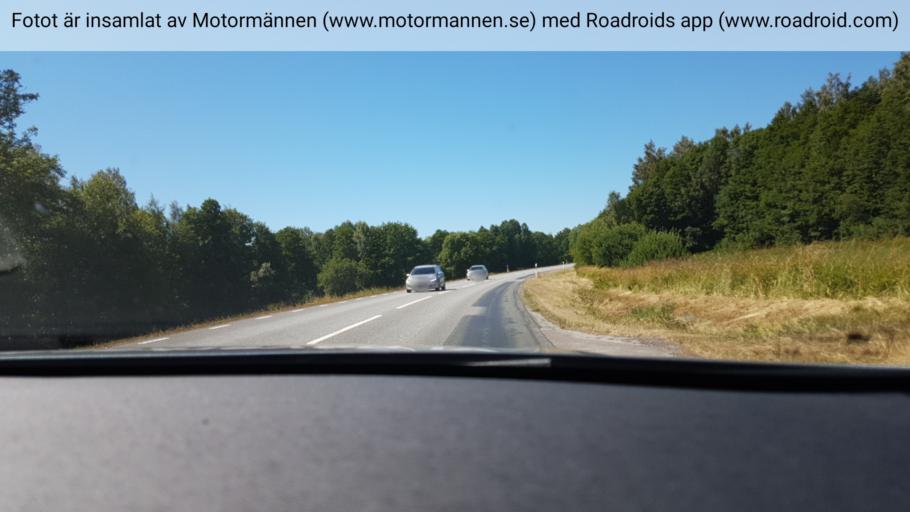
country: SE
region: Joenkoeping
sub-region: Jonkopings Kommun
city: Asa
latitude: 58.0011
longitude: 14.7230
